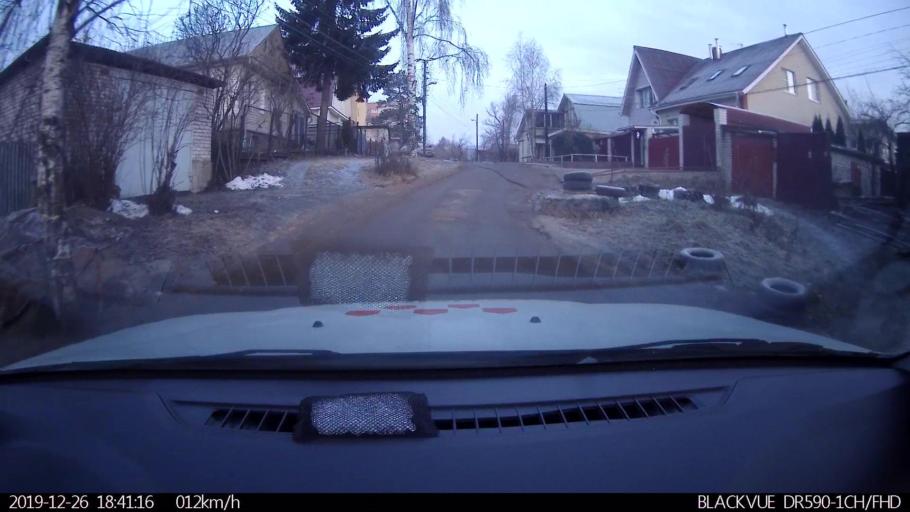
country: RU
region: Nizjnij Novgorod
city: Nizhniy Novgorod
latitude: 56.3151
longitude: 44.0355
